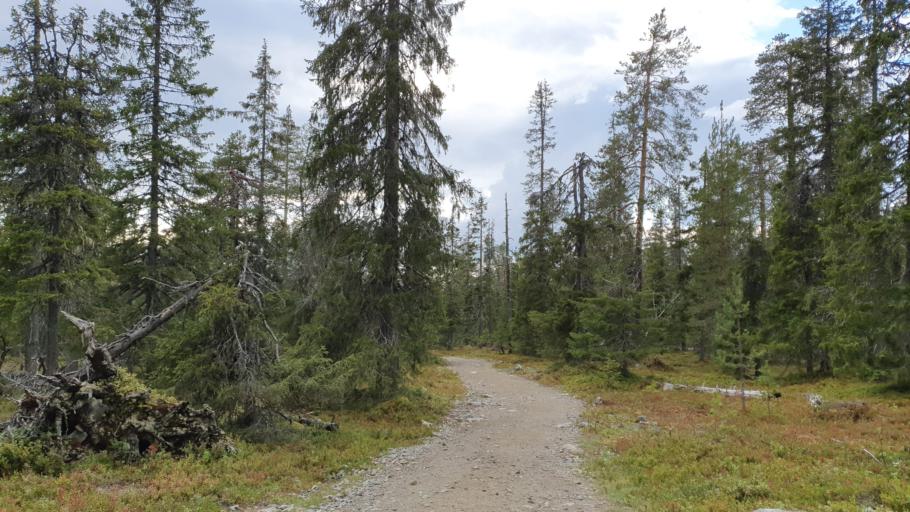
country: FI
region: Lapland
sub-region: Tunturi-Lappi
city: Kolari
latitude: 67.6179
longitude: 24.2461
